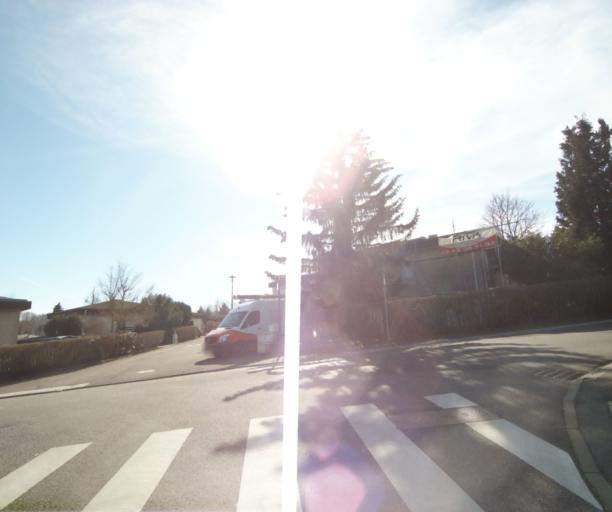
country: FR
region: Lorraine
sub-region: Departement de Meurthe-et-Moselle
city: Villers-les-Nancy
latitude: 48.6635
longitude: 6.1400
